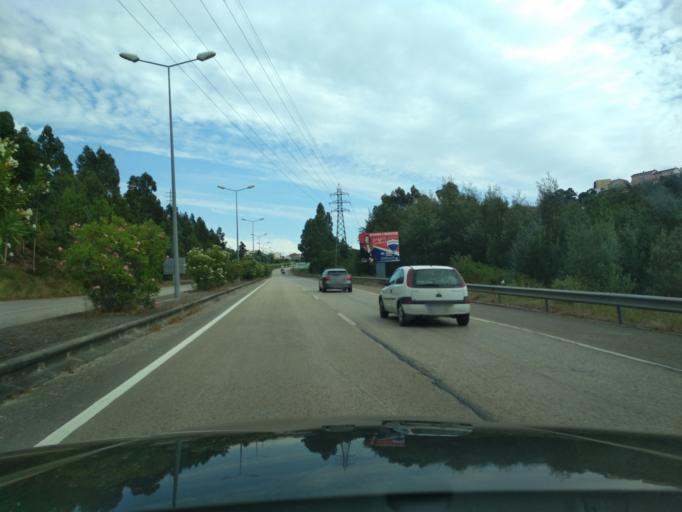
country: PT
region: Coimbra
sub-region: Coimbra
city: Coimbra
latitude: 40.2202
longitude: -8.3957
